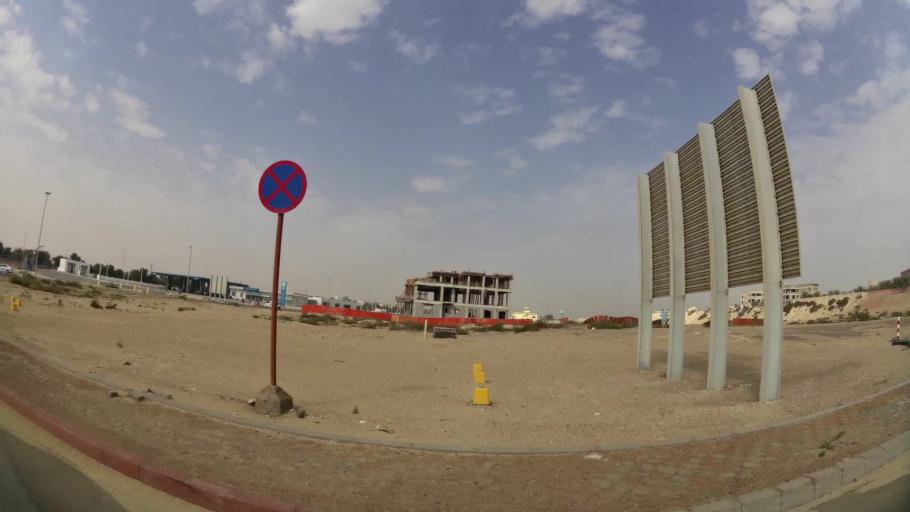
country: AE
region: Abu Dhabi
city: Abu Dhabi
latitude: 24.2721
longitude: 54.6647
